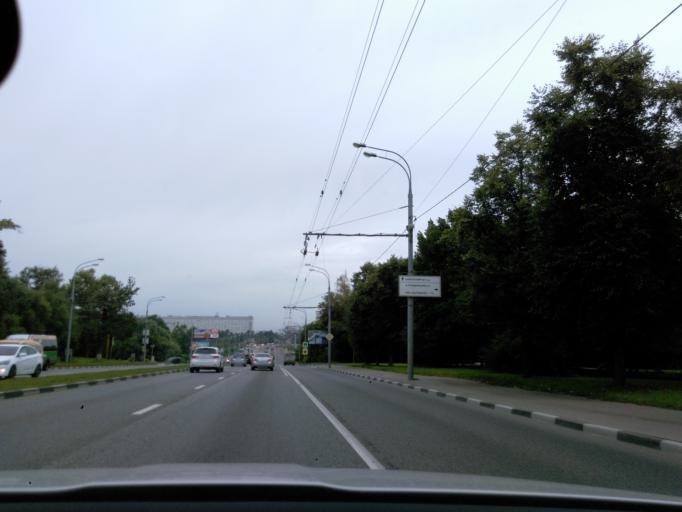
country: RU
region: Moscow
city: Tsaritsyno
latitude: 55.6108
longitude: 37.6637
